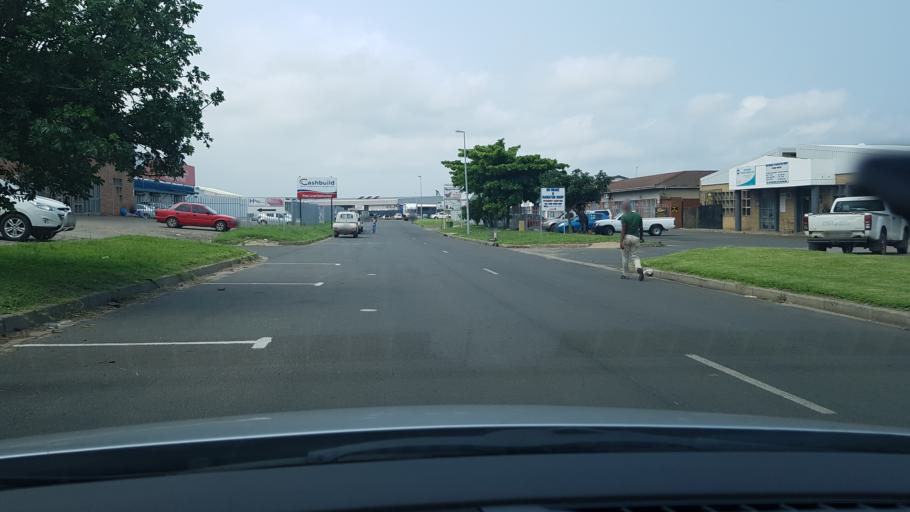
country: ZA
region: KwaZulu-Natal
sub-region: uThungulu District Municipality
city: Richards Bay
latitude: -28.7459
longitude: 32.0481
